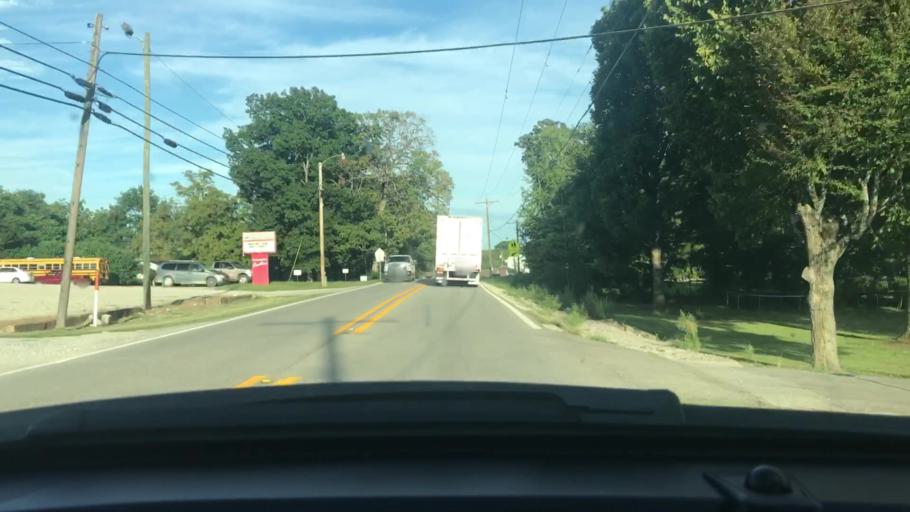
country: US
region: Arkansas
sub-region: Randolph County
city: Pocahontas
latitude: 36.2038
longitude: -91.1808
